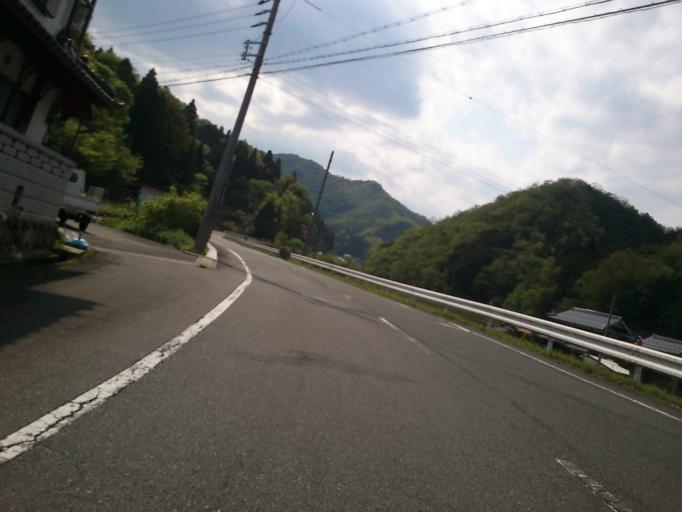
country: JP
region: Kyoto
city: Fukuchiyama
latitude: 35.2918
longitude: 135.0219
